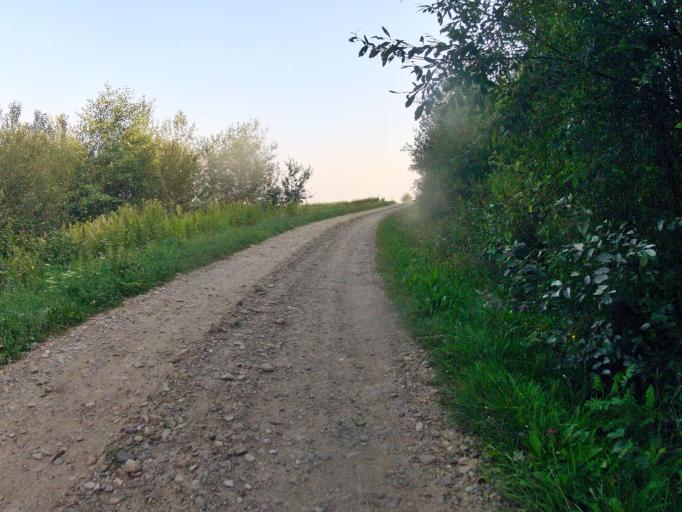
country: PL
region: Subcarpathian Voivodeship
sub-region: Powiat jasielski
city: Brzyska
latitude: 49.7880
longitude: 21.3870
